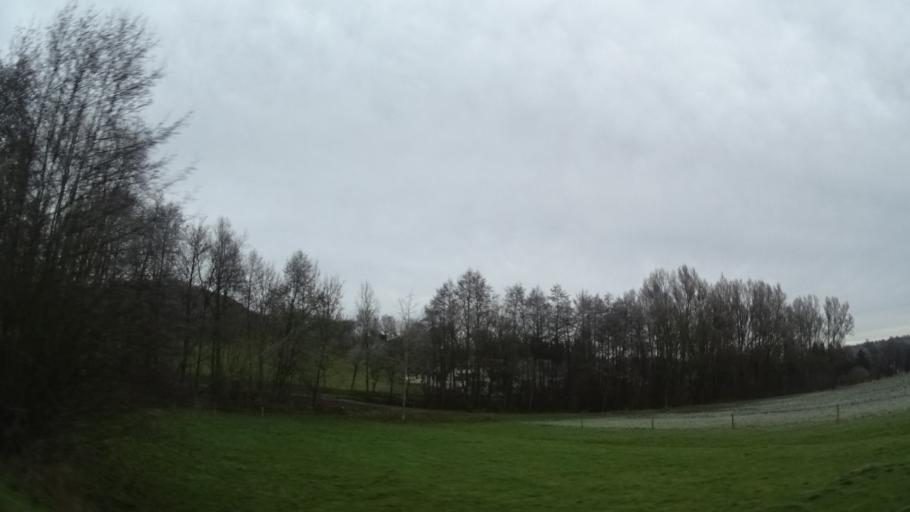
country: DE
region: Hesse
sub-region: Regierungsbezirk Kassel
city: Rasdorf
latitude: 50.7175
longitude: 9.8898
